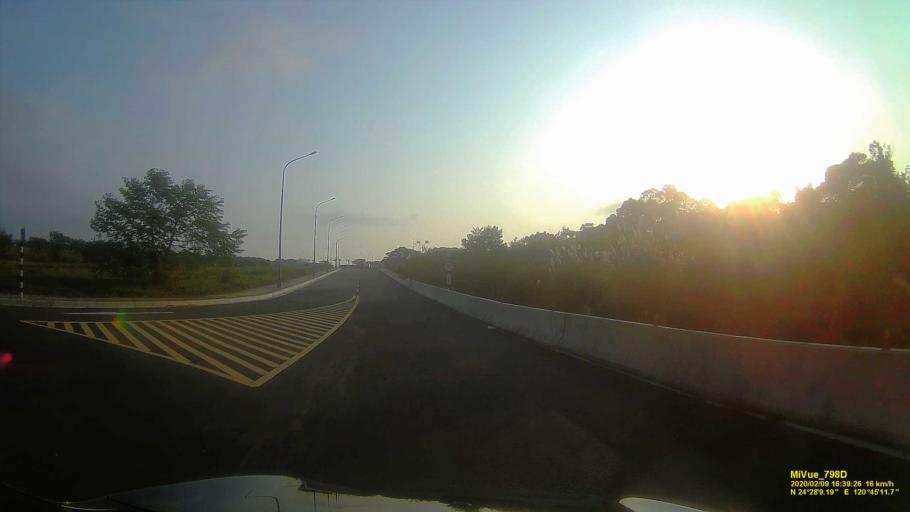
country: TW
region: Taiwan
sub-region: Miaoli
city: Miaoli
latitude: 24.4691
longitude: 120.7532
